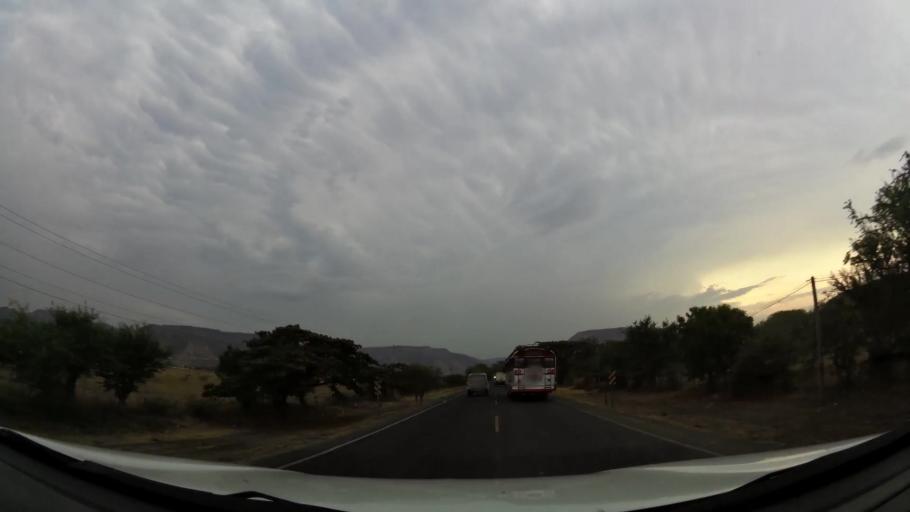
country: NI
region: Matagalpa
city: Ciudad Dario
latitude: 12.9081
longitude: -86.1740
